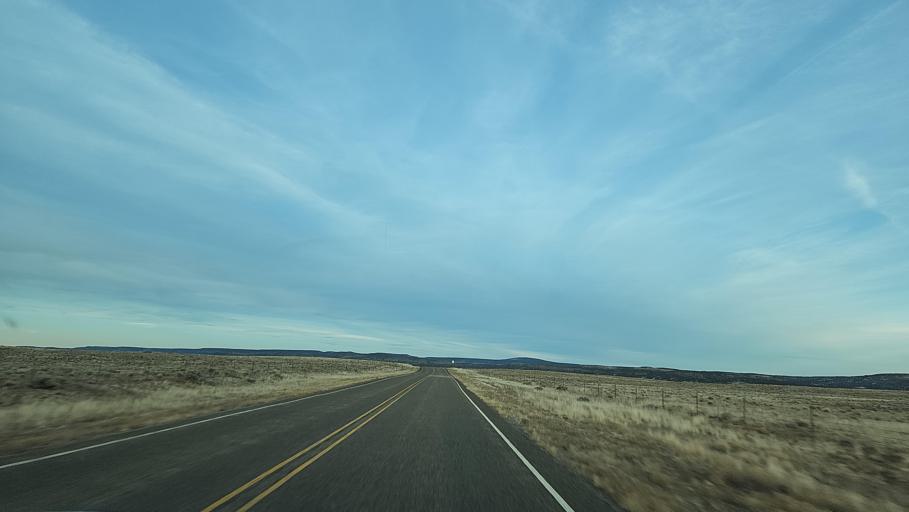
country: US
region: New Mexico
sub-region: Cibola County
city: Grants
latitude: 34.6982
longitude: -108.0443
